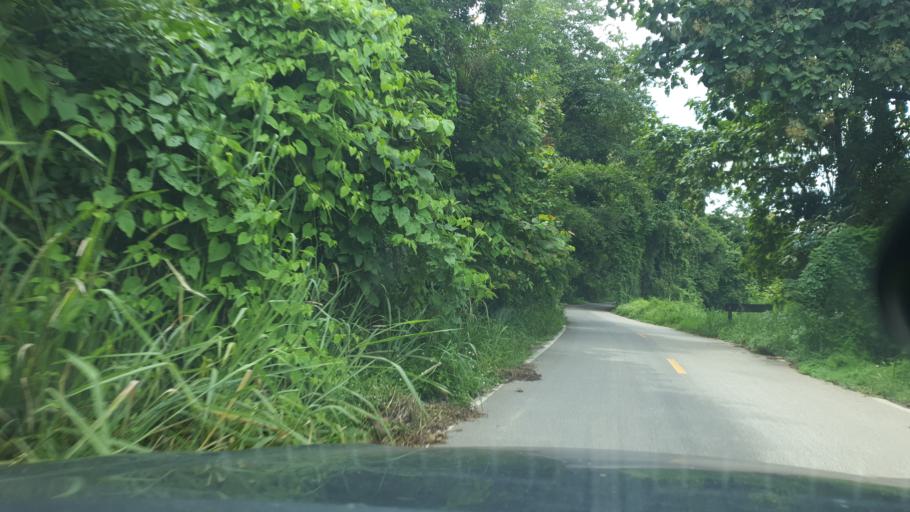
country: TH
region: Lamphun
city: Mae Tha
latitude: 18.5267
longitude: 99.2603
